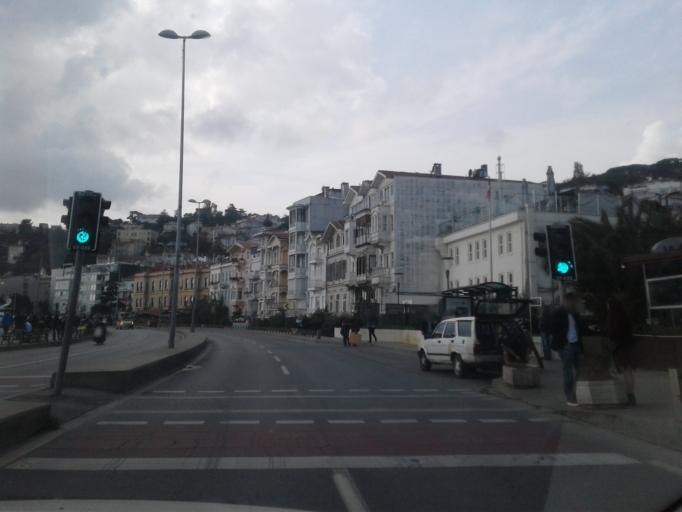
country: TR
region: Istanbul
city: UEskuedar
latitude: 41.0671
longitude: 29.0437
